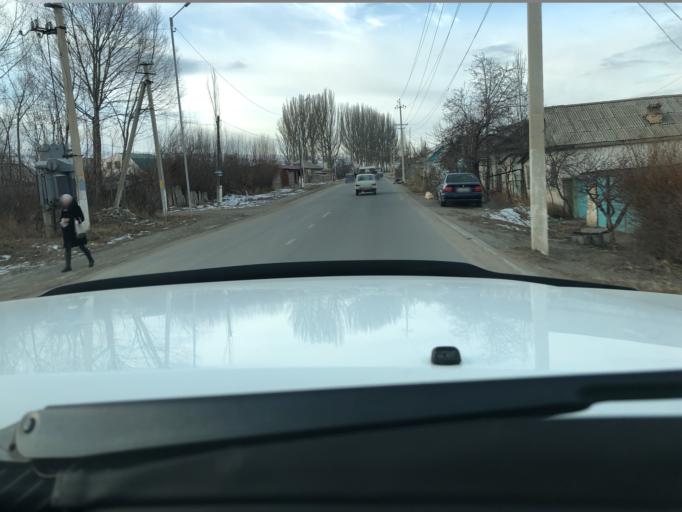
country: KG
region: Ysyk-Koel
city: Karakol
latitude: 42.4722
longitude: 78.3853
